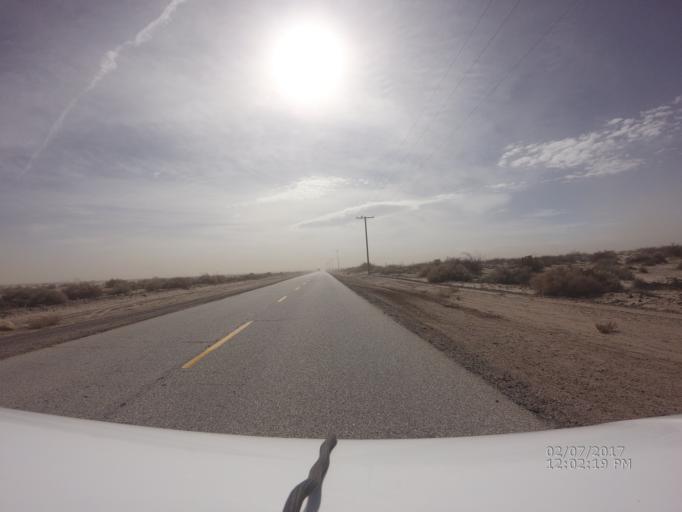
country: US
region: California
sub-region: Los Angeles County
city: Lake Los Angeles
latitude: 34.6957
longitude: -117.8807
